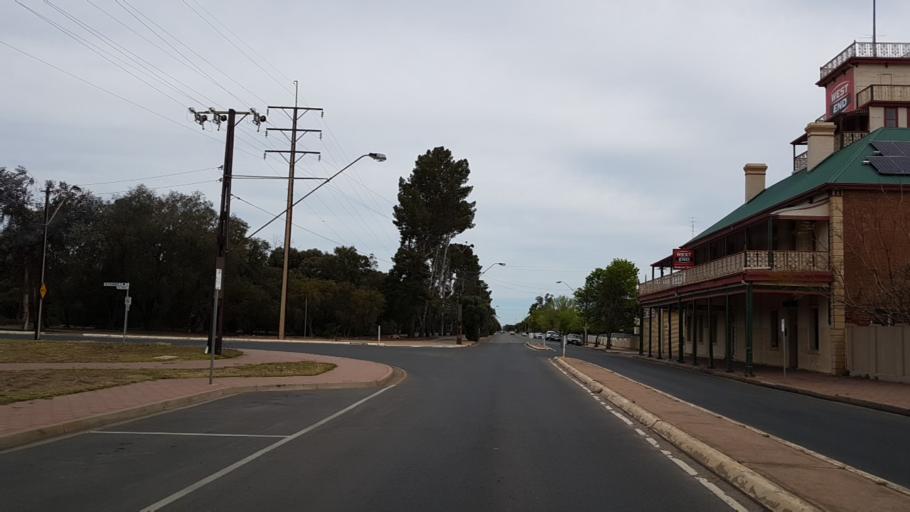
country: AU
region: South Australia
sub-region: Port Pirie City and Dists
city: Port Pirie
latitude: -33.1778
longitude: 138.0039
